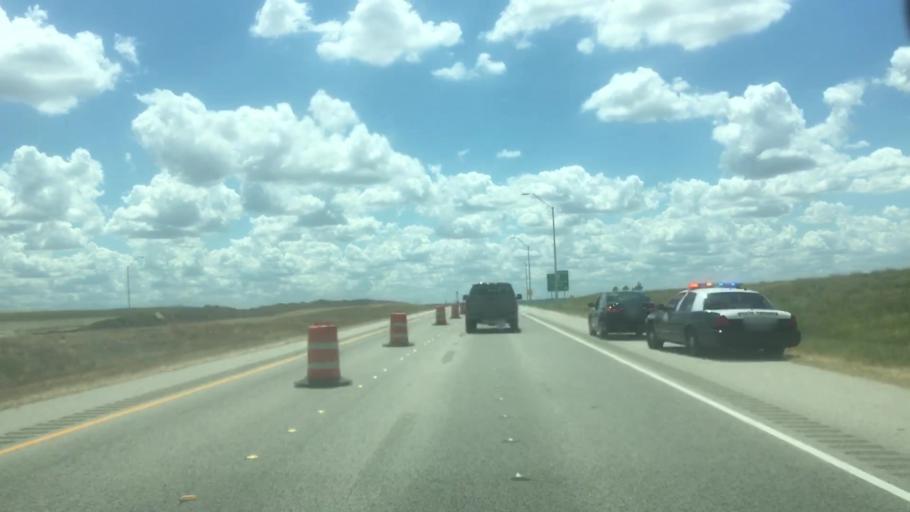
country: US
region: Texas
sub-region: Caldwell County
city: Martindale
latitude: 29.7906
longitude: -97.7844
